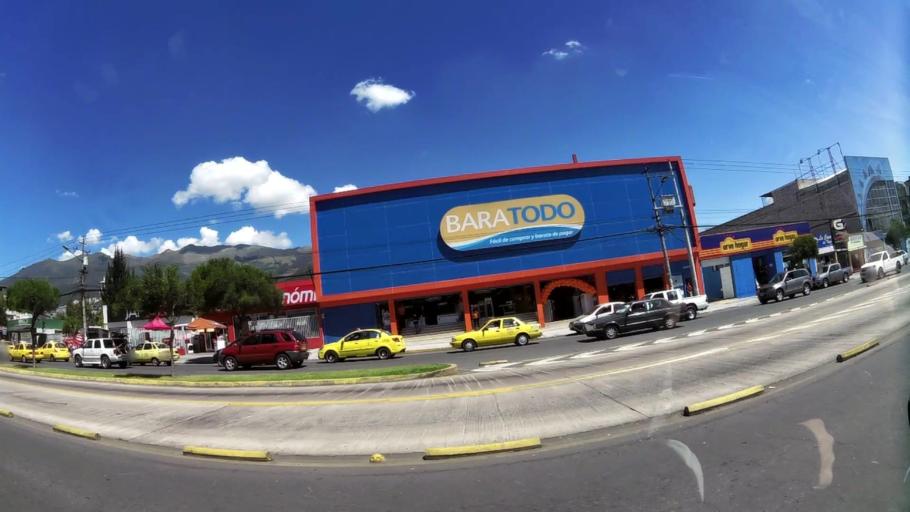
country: EC
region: Pichincha
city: Quito
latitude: -0.1260
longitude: -78.4940
